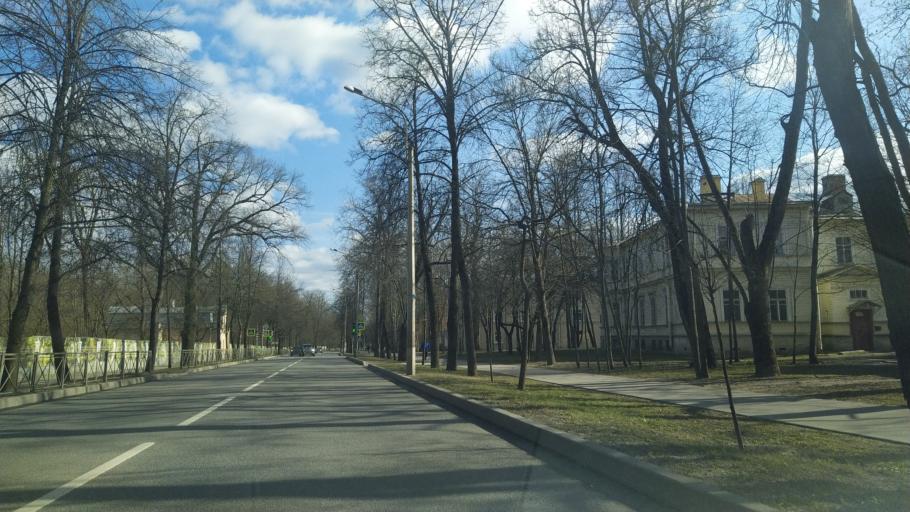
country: RU
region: St.-Petersburg
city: Pushkin
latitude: 59.7095
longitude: 30.4136
